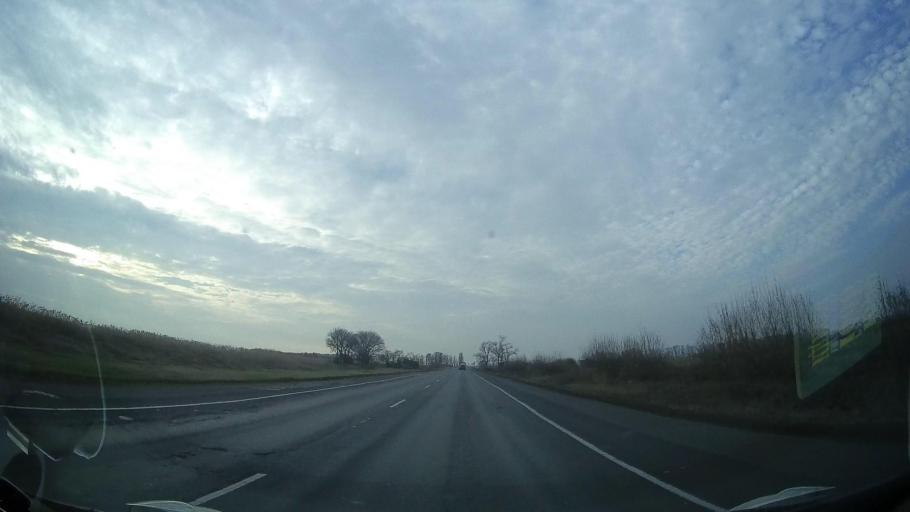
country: RU
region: Rostov
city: Starocherkasskaya
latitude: 47.1547
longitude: 40.1721
